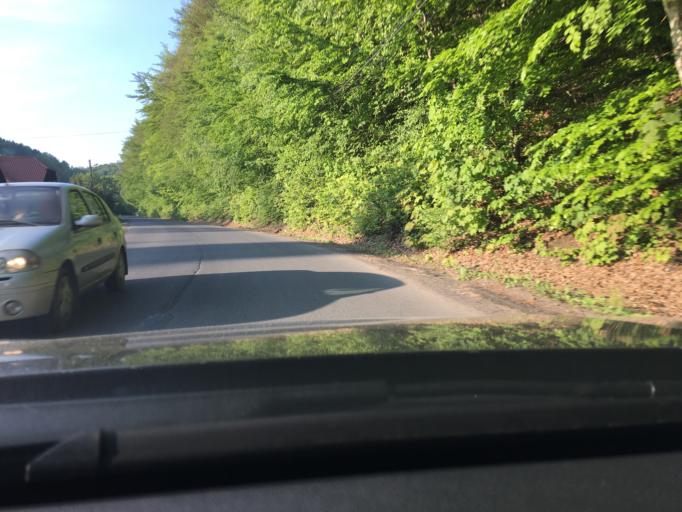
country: PL
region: Lesser Poland Voivodeship
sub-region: Powiat krakowski
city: Jerzmanowice
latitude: 50.1901
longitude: 19.7216
